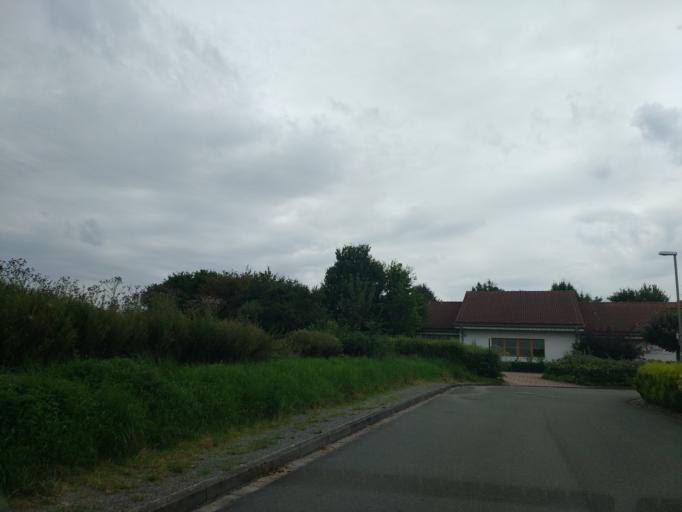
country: DE
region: North Rhine-Westphalia
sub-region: Regierungsbezirk Detmold
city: Bad Meinberg
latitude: 51.9159
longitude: 9.0335
